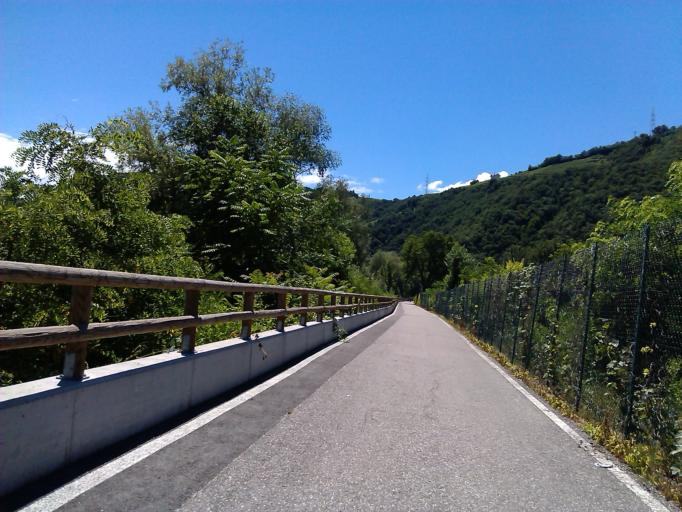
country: IT
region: Trentino-Alto Adige
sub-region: Bolzano
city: Cornaiano
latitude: 46.4658
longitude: 11.3046
